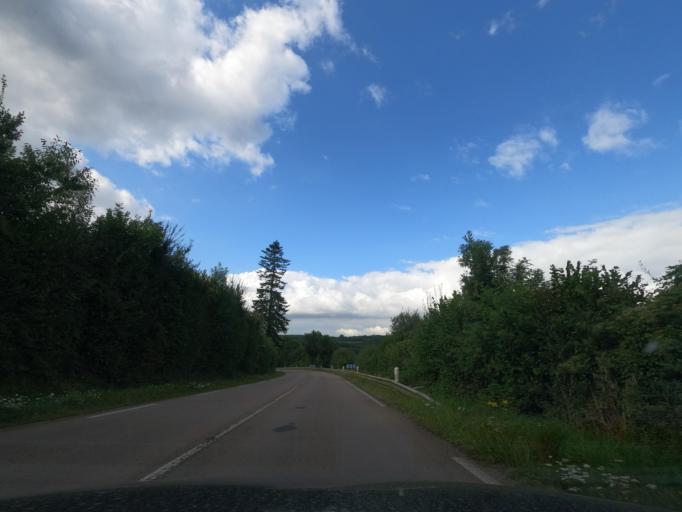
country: FR
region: Lower Normandy
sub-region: Departement de l'Orne
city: Gace
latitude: 48.8043
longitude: 0.3108
